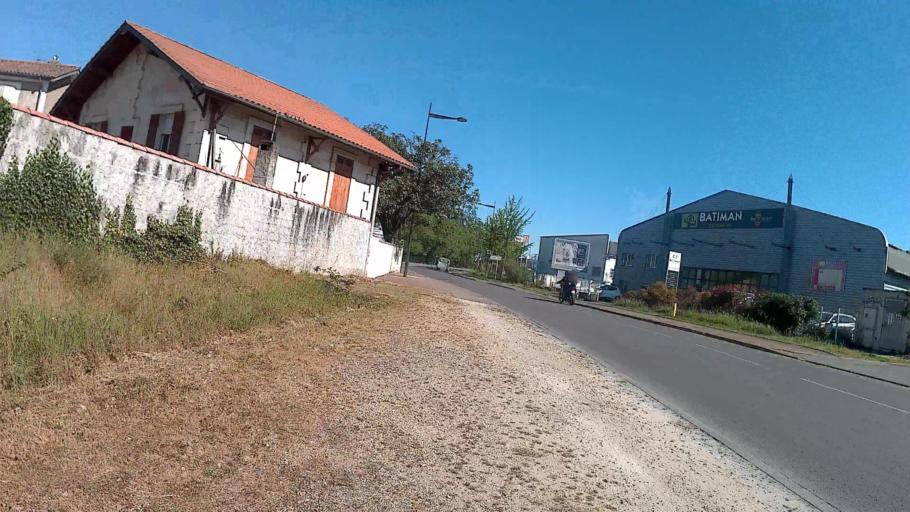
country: FR
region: Aquitaine
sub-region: Departement de la Gironde
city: Begles
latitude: 44.7954
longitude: -0.5416
